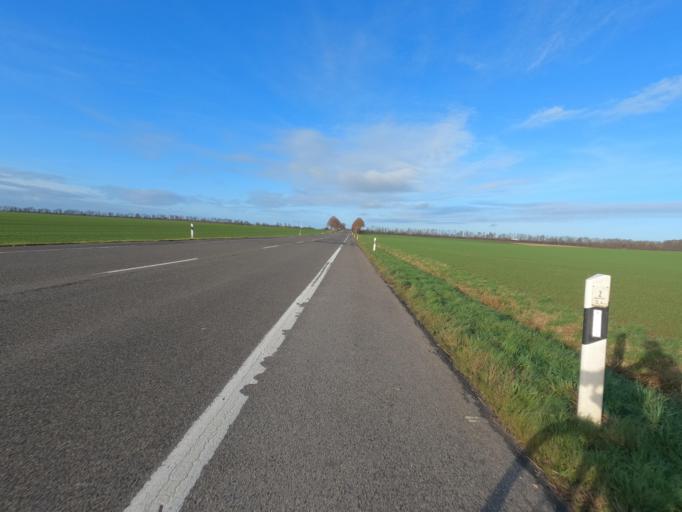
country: DE
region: North Rhine-Westphalia
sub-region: Regierungsbezirk Koln
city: Titz
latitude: 50.9984
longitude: 6.4064
